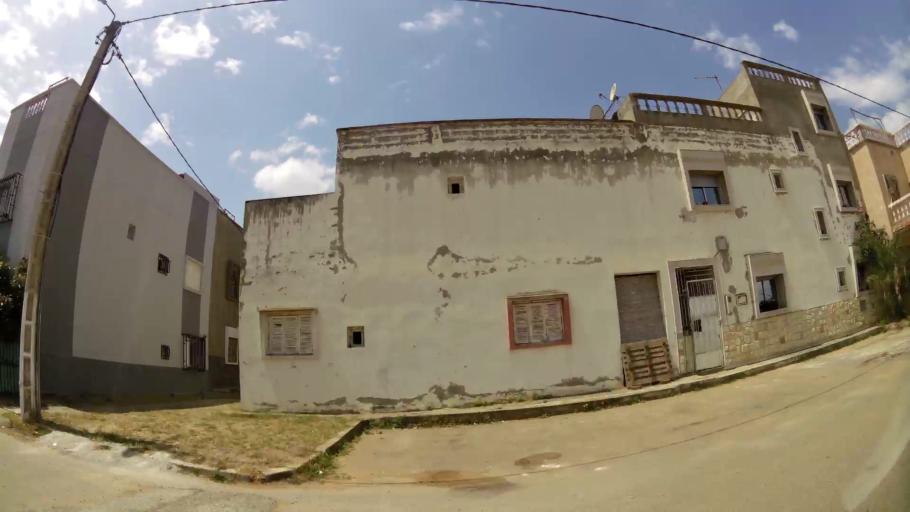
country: MA
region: Gharb-Chrarda-Beni Hssen
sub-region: Kenitra Province
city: Kenitra
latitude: 34.0145
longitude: -6.5315
